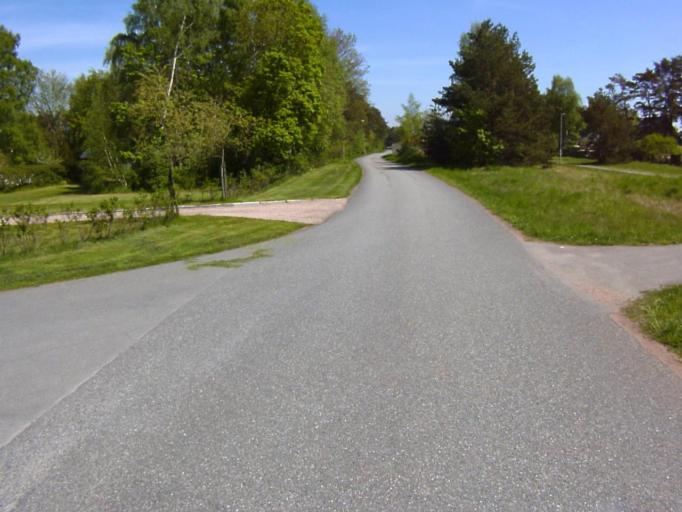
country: SE
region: Skane
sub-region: Kristianstads Kommun
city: Degeberga
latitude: 55.9002
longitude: 14.0920
